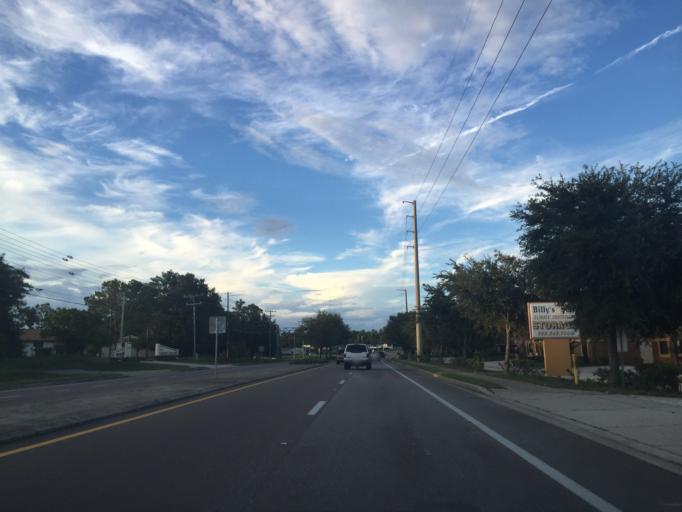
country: US
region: Florida
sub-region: Lake County
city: Tavares
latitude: 28.7865
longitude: -81.7479
